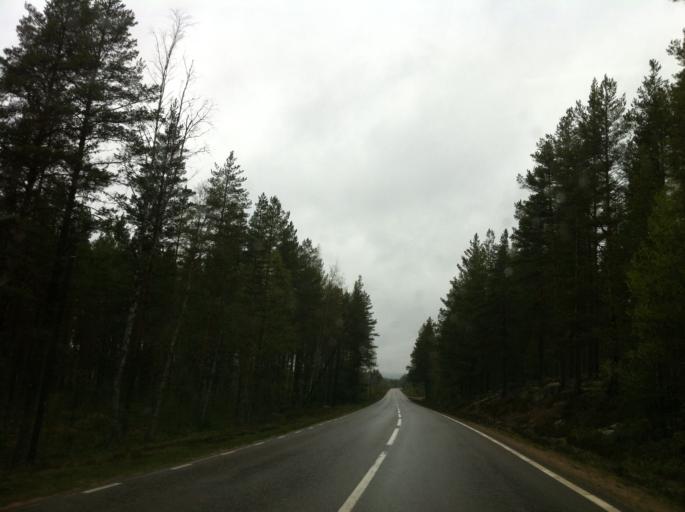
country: SE
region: Jaemtland
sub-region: Harjedalens Kommun
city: Sveg
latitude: 62.1463
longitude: 13.9372
